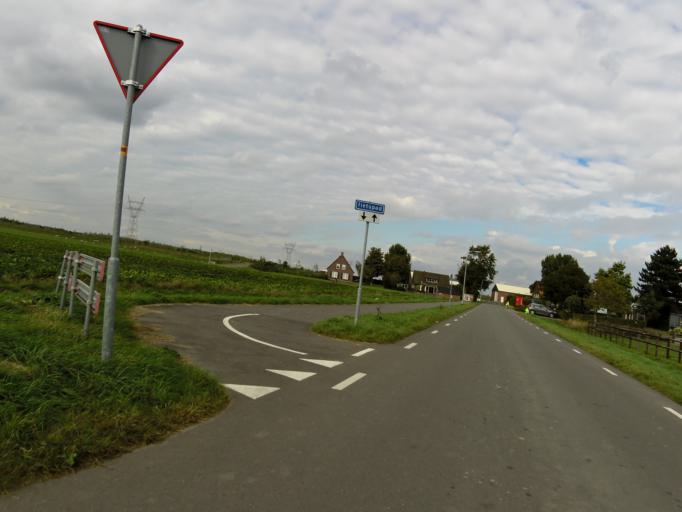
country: NL
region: South Holland
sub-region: Gemeente Rijnwoude
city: Benthuizen
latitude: 52.0588
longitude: 4.5757
